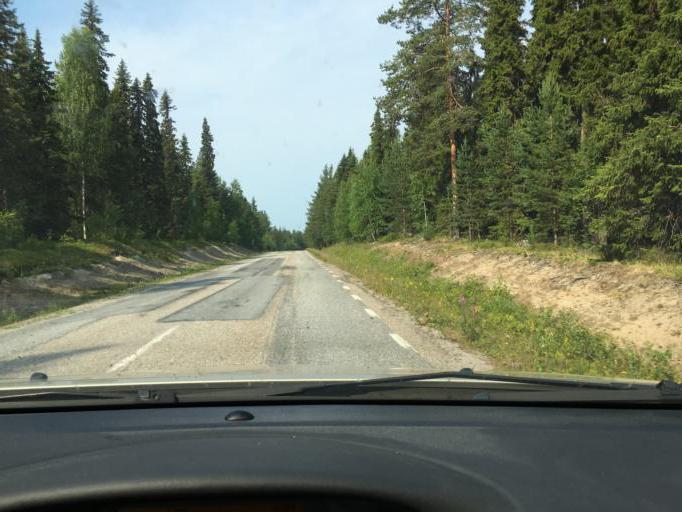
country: SE
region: Norrbotten
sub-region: Kalix Kommun
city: Rolfs
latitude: 65.7704
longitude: 22.9647
